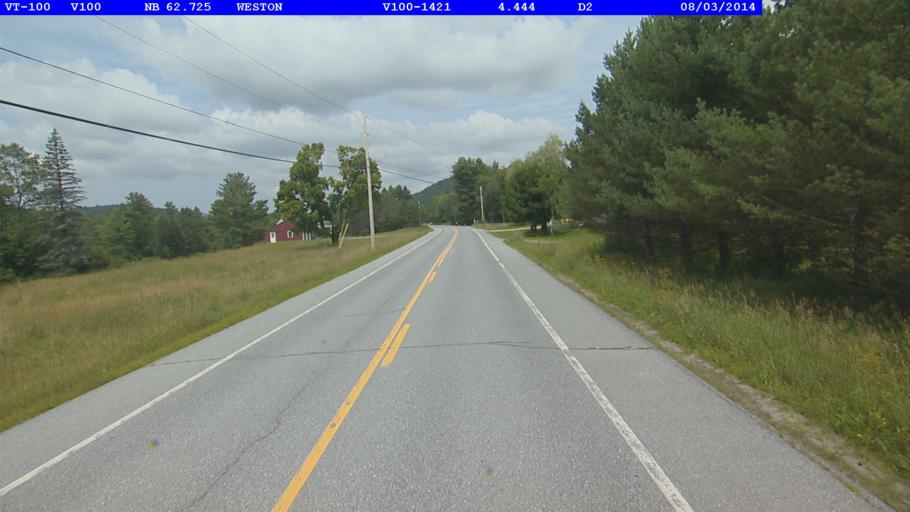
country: US
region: Vermont
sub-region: Windsor County
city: Chester
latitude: 43.3082
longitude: -72.7867
